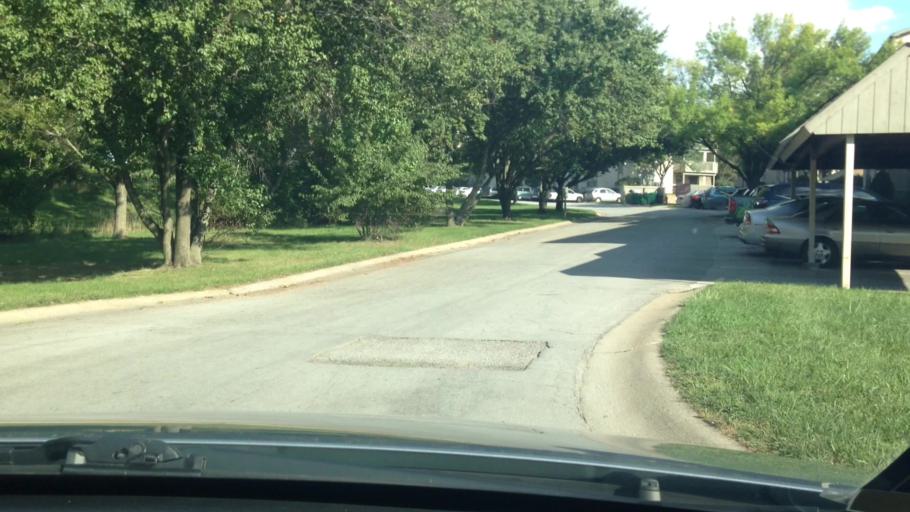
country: US
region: Missouri
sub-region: Clay County
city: Gladstone
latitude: 39.1852
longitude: -94.5794
